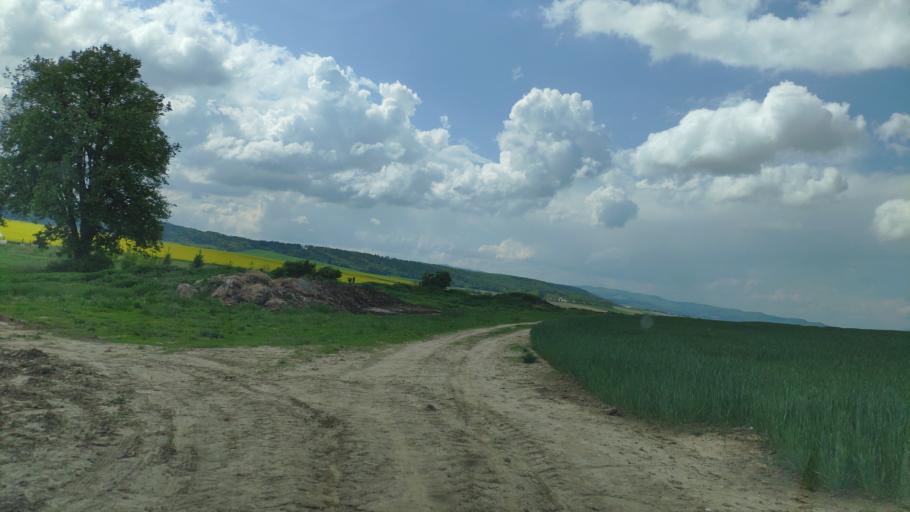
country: SK
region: Presovsky
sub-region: Okres Presov
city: Presov
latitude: 49.0294
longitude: 21.1693
